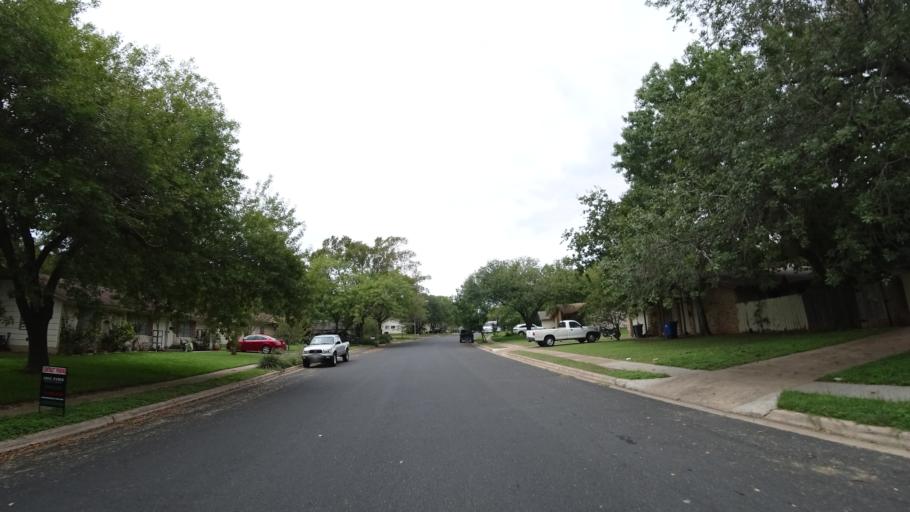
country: US
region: Texas
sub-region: Travis County
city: Rollingwood
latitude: 30.2143
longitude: -97.7821
